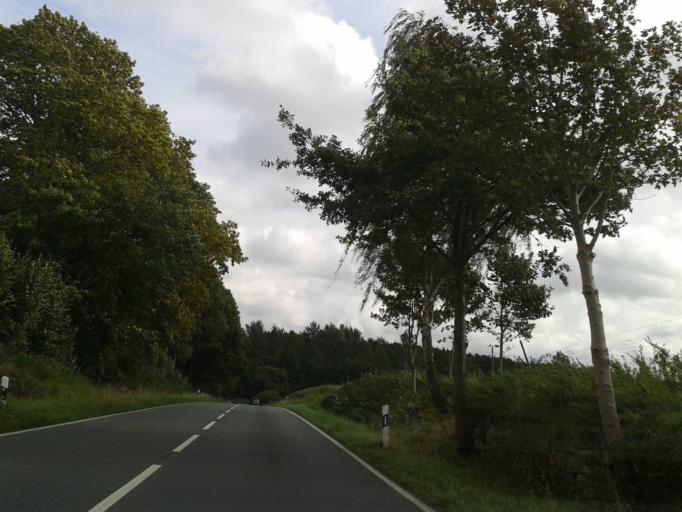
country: DE
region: North Rhine-Westphalia
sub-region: Regierungsbezirk Detmold
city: Lemgo
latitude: 52.0263
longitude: 8.9429
